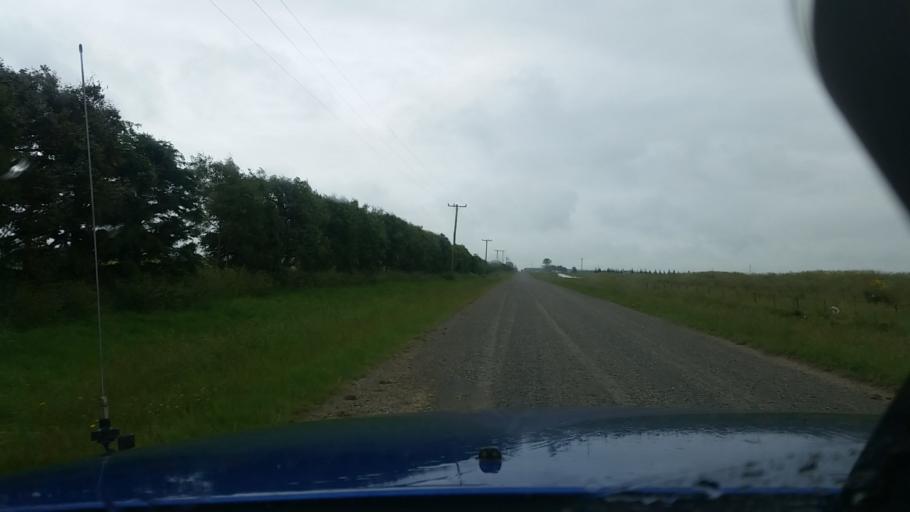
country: NZ
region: Canterbury
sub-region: Ashburton District
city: Tinwald
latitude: -43.9027
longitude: 171.5905
